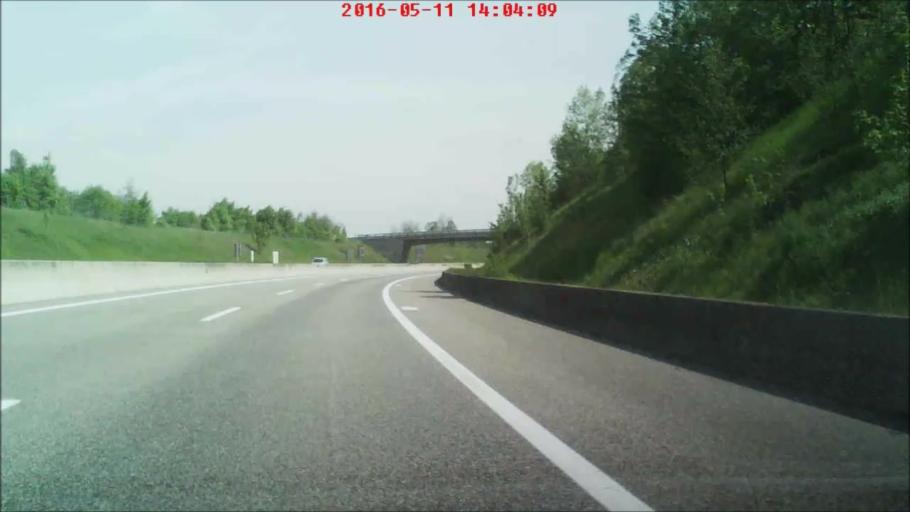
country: AT
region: Upper Austria
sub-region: Wels-Land
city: Steinhaus
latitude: 48.1368
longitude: 13.9998
